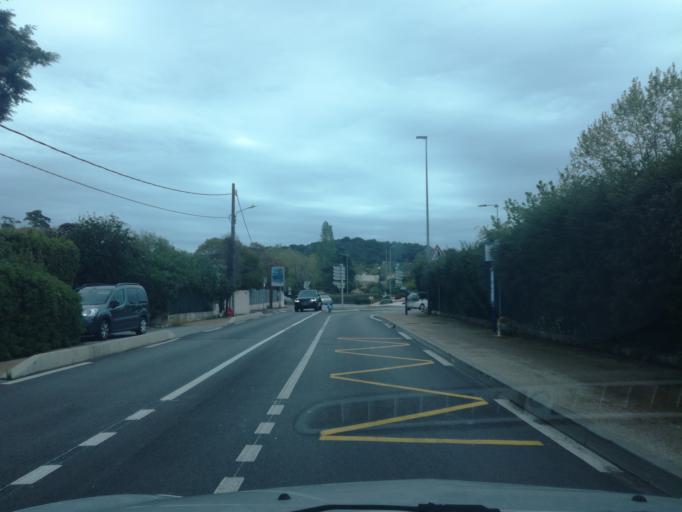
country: FR
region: Provence-Alpes-Cote d'Azur
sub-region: Departement des Alpes-Maritimes
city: Mougins
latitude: 43.6025
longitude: 7.0138
